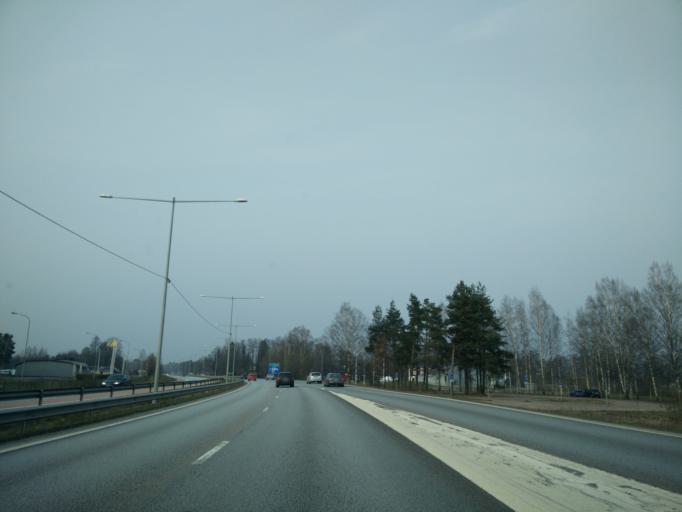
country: SE
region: Vaermland
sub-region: Karlstads Kommun
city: Karlstad
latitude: 59.3865
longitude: 13.4916
